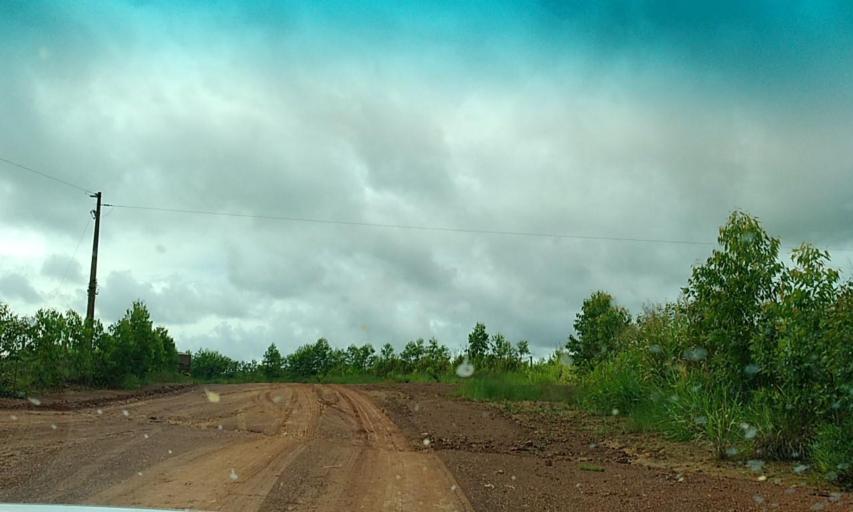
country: BR
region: Para
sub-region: Altamira
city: Altamira
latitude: -3.0615
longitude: -51.7198
